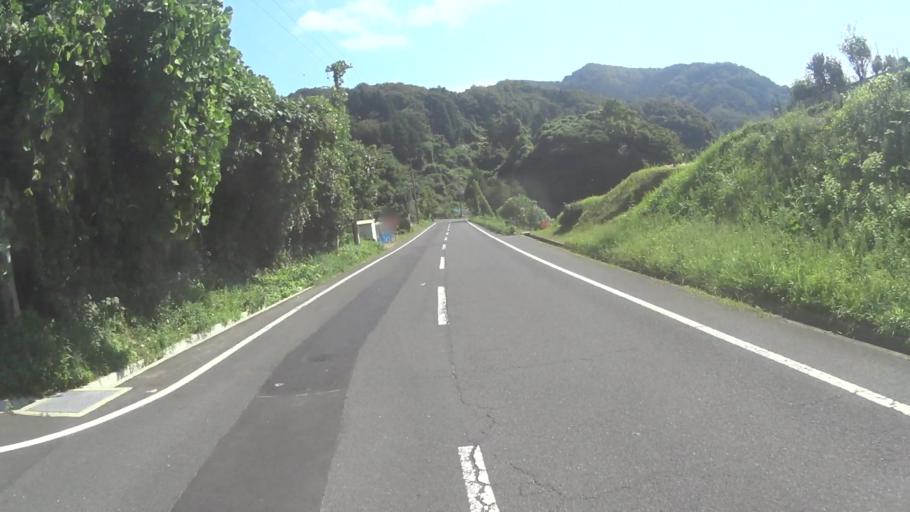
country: JP
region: Kyoto
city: Miyazu
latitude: 35.6765
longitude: 135.2943
